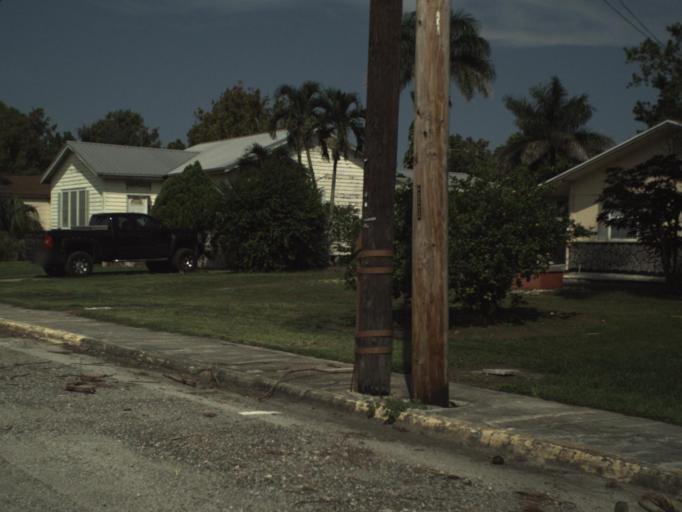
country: US
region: Florida
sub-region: Palm Beach County
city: Pahokee
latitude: 26.8153
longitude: -80.6804
